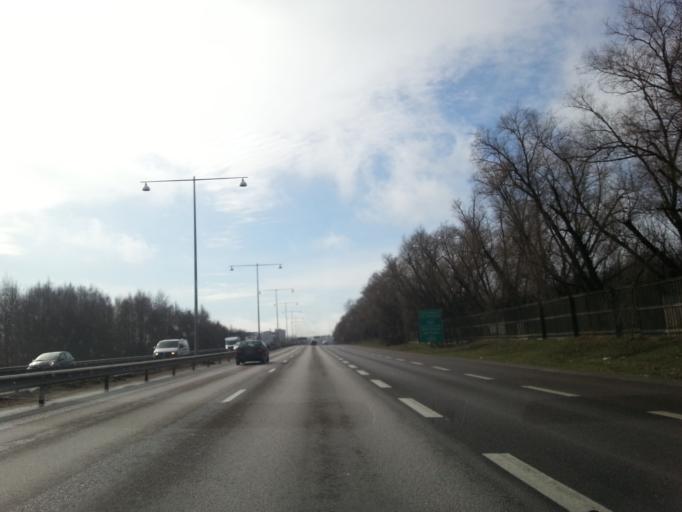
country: SE
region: Vaestra Goetaland
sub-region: Goteborg
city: Goeteborg
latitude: 57.7388
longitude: 11.9867
